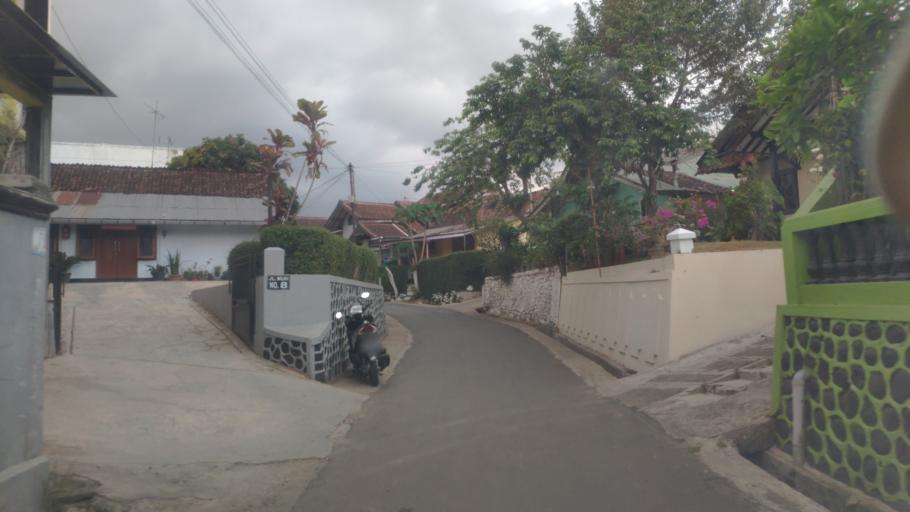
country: ID
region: Central Java
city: Wonosobo
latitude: -7.3931
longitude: 109.7080
